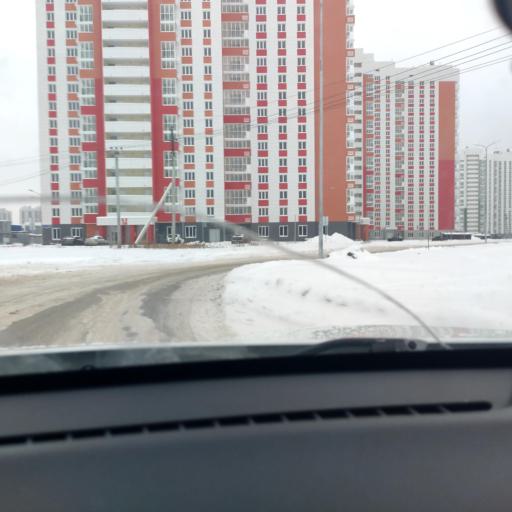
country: RU
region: Tatarstan
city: Osinovo
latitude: 55.8615
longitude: 48.8981
